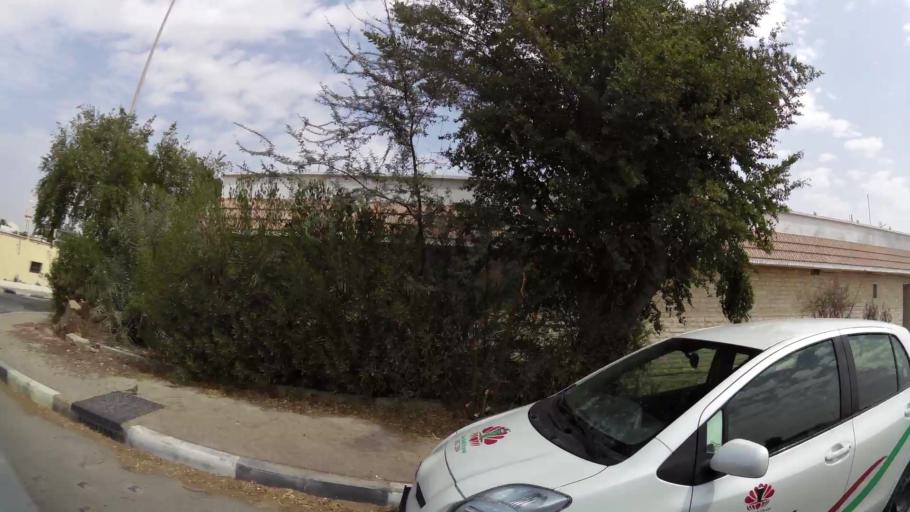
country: AE
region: Abu Dhabi
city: Abu Dhabi
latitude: 24.3016
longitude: 54.6220
